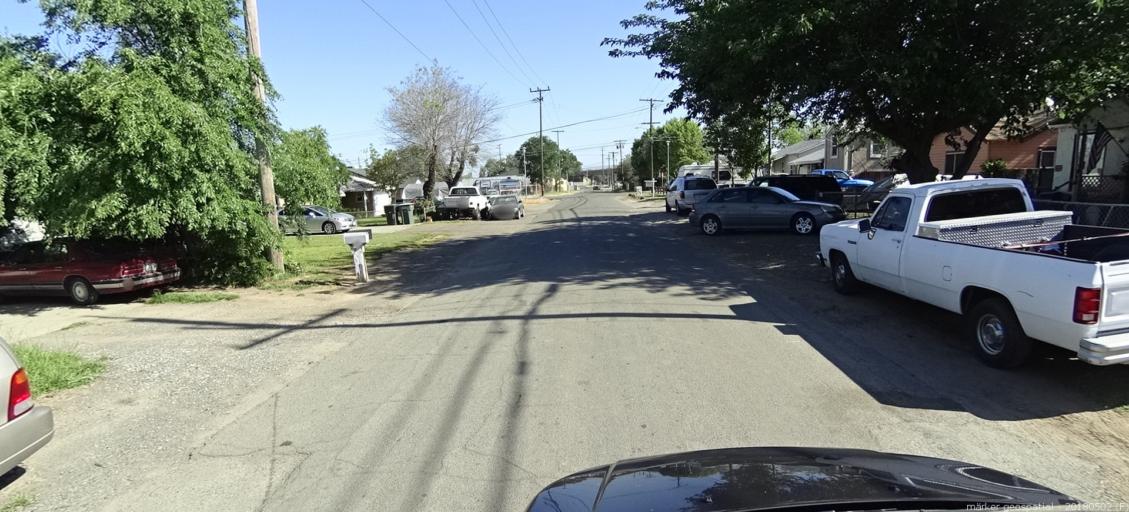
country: US
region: California
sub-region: Sacramento County
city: Arden-Arcade
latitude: 38.6194
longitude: -121.4231
